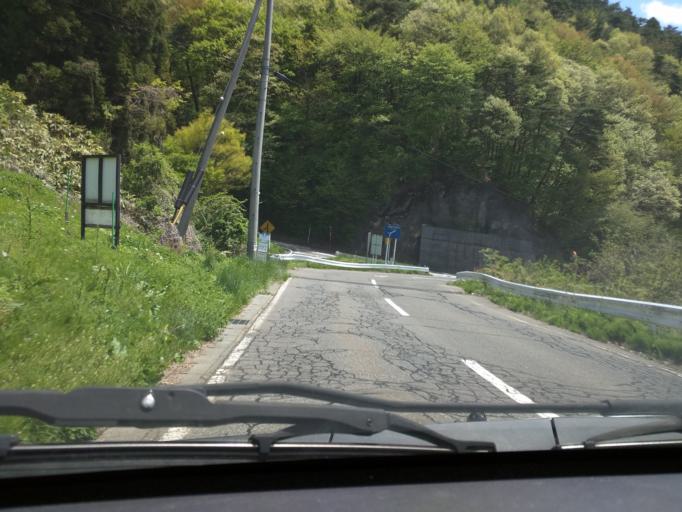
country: JP
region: Nagano
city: Nagano-shi
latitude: 36.6785
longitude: 138.1721
